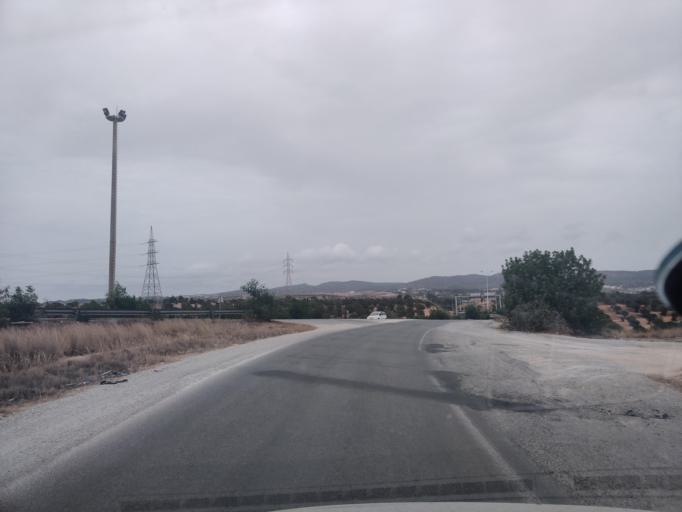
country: TN
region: Nabul
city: Al Hammamat
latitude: 36.4402
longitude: 10.5654
